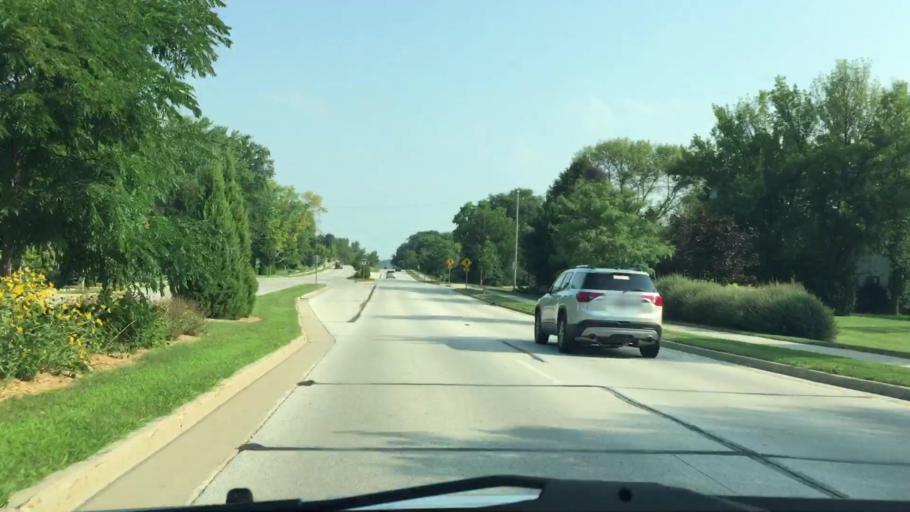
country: US
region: Wisconsin
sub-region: Waukesha County
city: Brookfield
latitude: 43.0196
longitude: -88.1269
